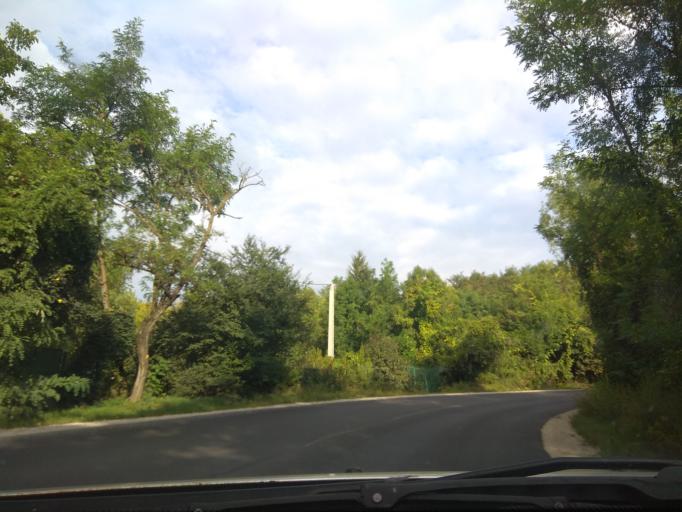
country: HU
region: Borsod-Abauj-Zemplen
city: Miskolc
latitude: 48.0866
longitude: 20.7507
